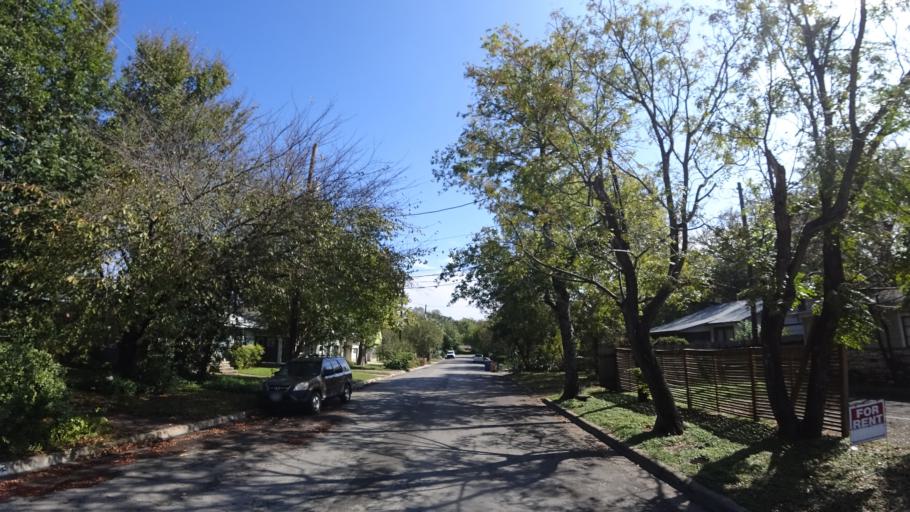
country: US
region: Texas
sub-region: Travis County
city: Rollingwood
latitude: 30.2545
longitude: -97.7713
